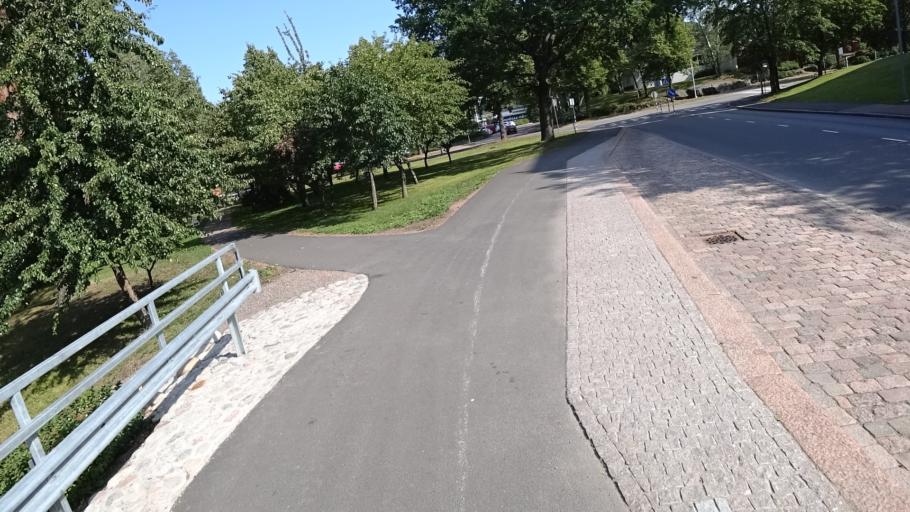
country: FI
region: Kymenlaakso
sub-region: Kotka-Hamina
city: Kotka
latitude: 60.4573
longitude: 26.9360
